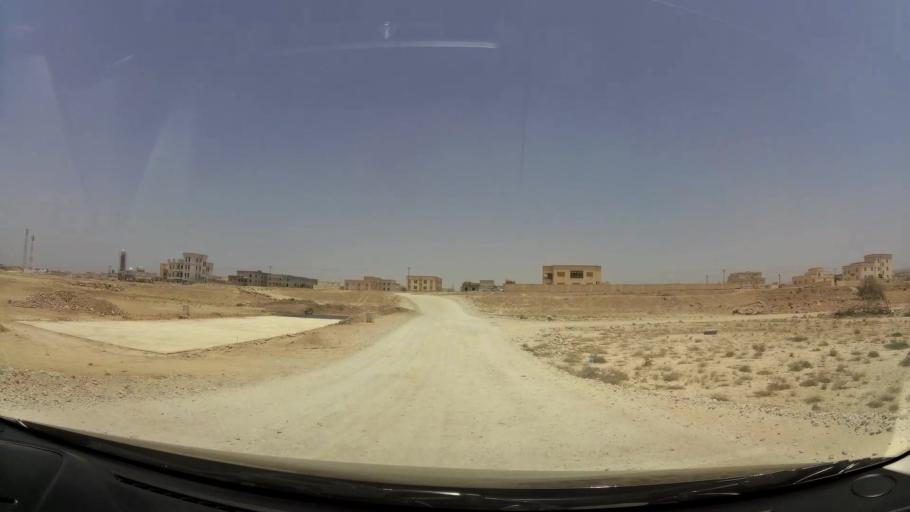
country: OM
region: Zufar
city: Salalah
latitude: 17.0895
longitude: 54.1632
